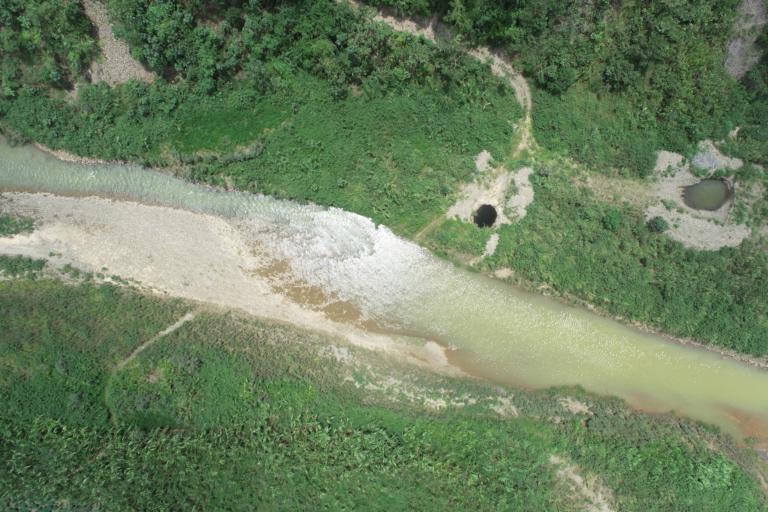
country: BO
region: La Paz
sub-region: Provincia Larecaja
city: Guanay
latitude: -15.7668
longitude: -67.6651
